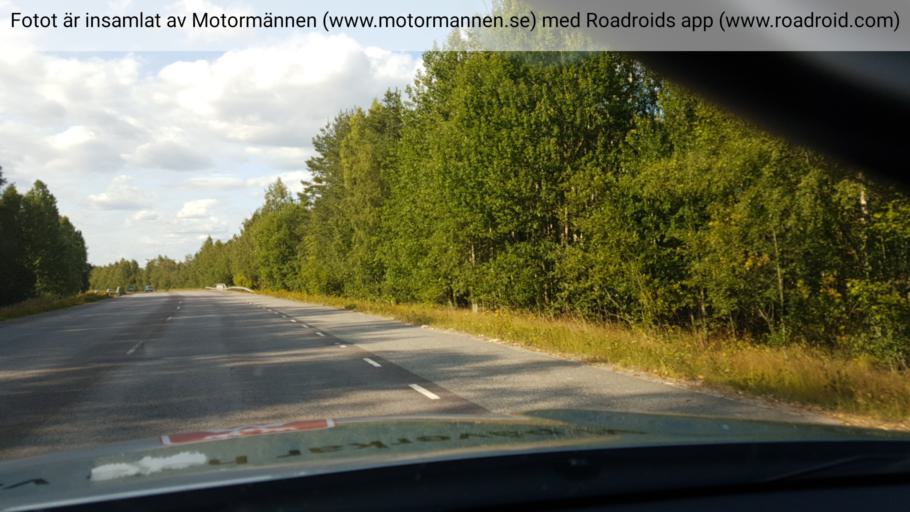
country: SE
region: Norrbotten
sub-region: Pitea Kommun
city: Pitea
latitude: 65.3066
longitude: 21.5065
